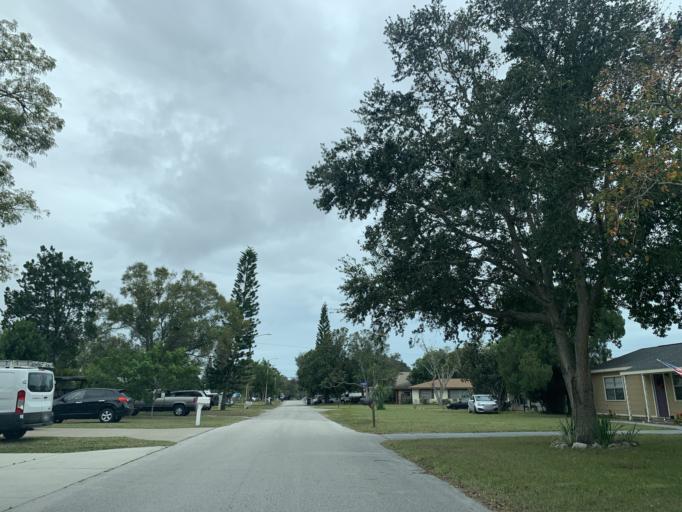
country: US
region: Florida
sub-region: Pinellas County
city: Belleair
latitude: 27.9414
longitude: -82.7864
